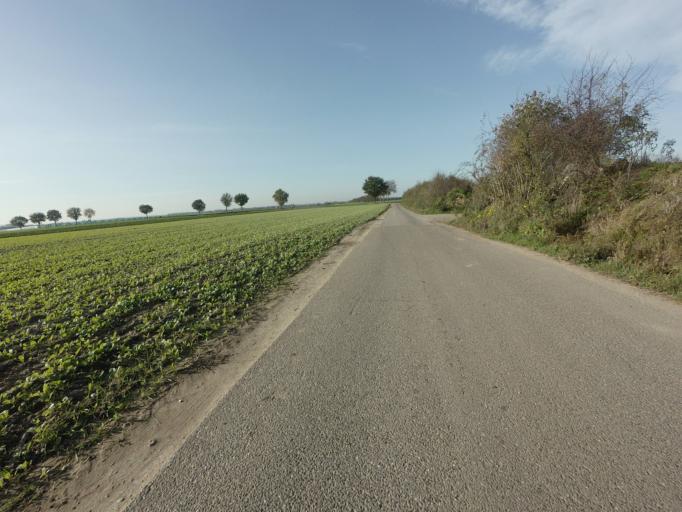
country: DE
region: North Rhine-Westphalia
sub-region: Regierungsbezirk Koln
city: Selfkant
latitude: 51.0446
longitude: 5.9242
